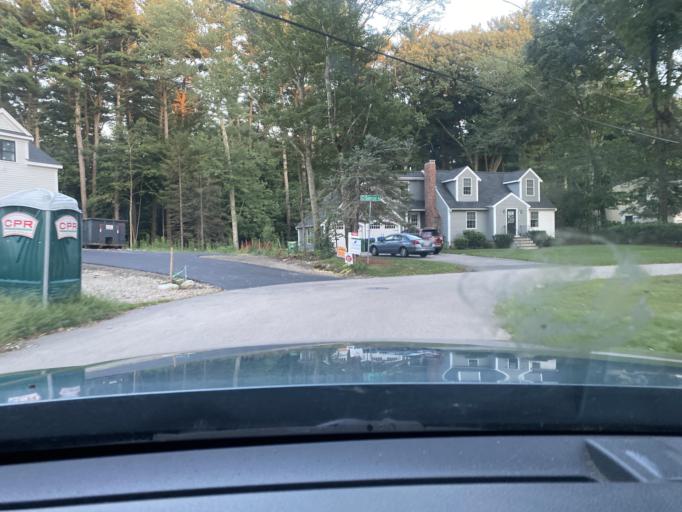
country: US
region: Massachusetts
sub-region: Norfolk County
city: Westwood
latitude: 42.2027
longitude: -71.2391
